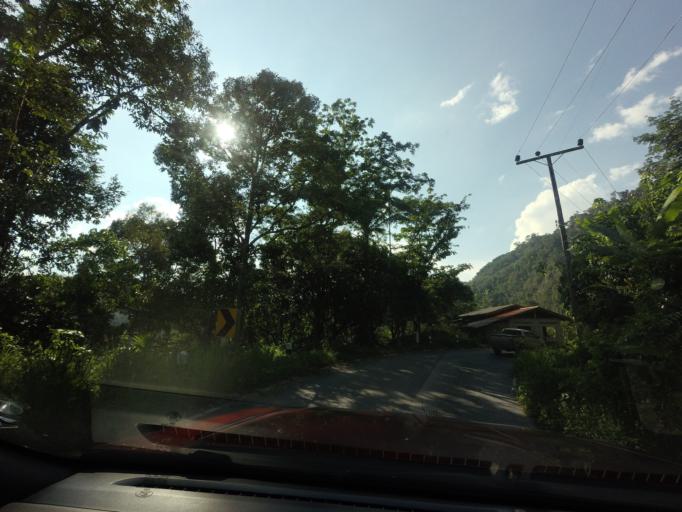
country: TH
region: Yala
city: Than To
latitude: 6.0838
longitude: 101.3280
